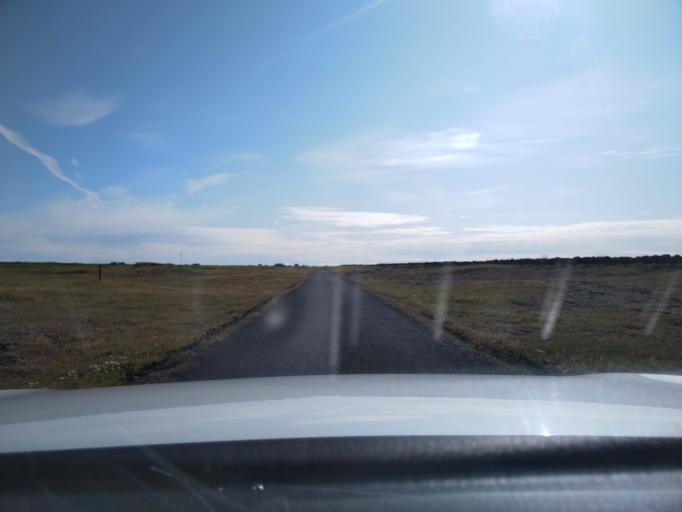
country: IS
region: South
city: THorlakshoefn
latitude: 63.8353
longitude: -21.7045
